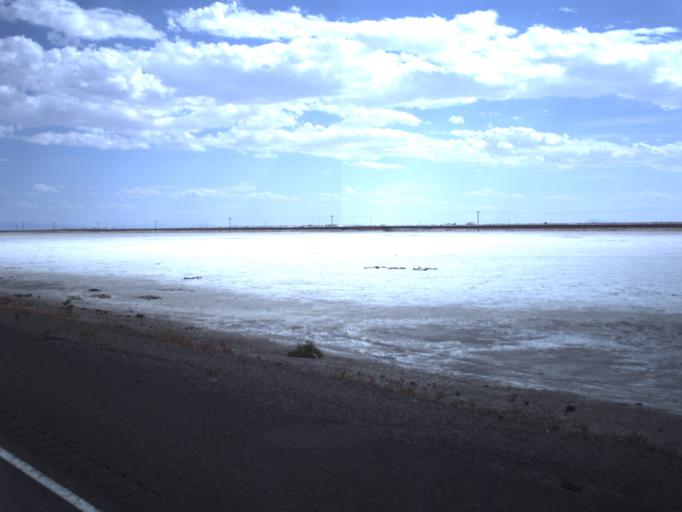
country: US
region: Utah
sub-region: Tooele County
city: Wendover
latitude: 40.7382
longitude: -113.8372
